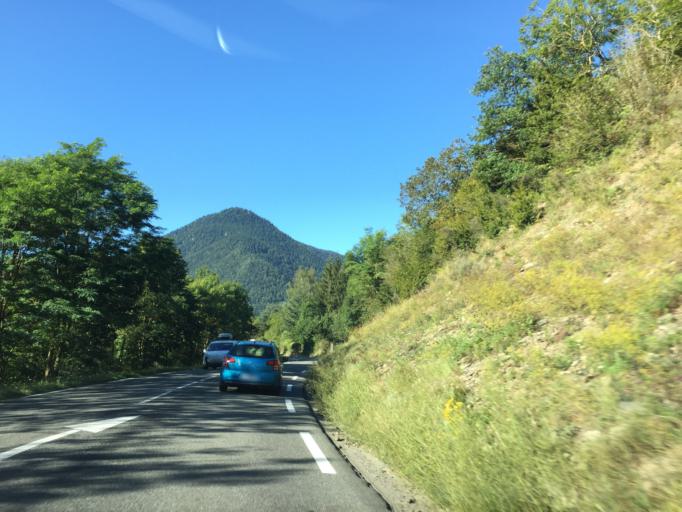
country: FR
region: Midi-Pyrenees
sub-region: Departement des Hautes-Pyrenees
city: Saint-Lary-Soulan
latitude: 42.8777
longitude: 0.3455
